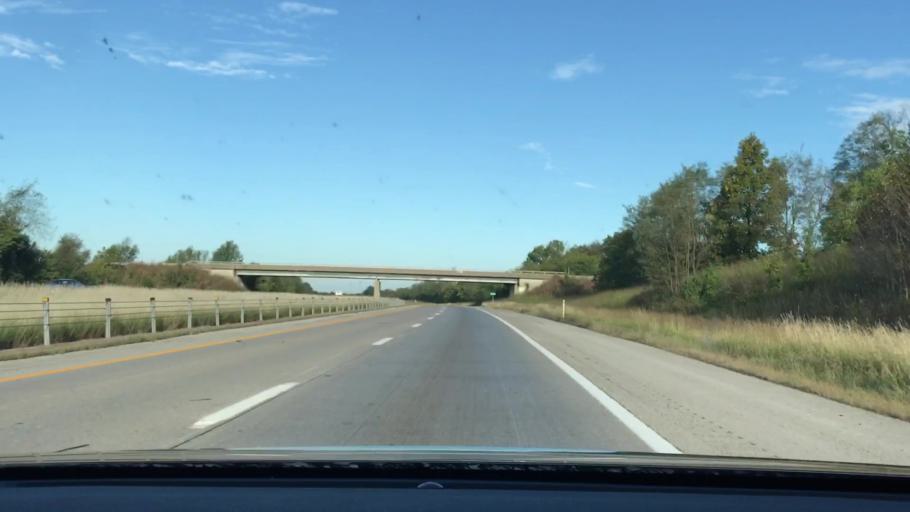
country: US
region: Kentucky
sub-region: Christian County
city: Hopkinsville
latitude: 36.7868
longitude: -87.5837
